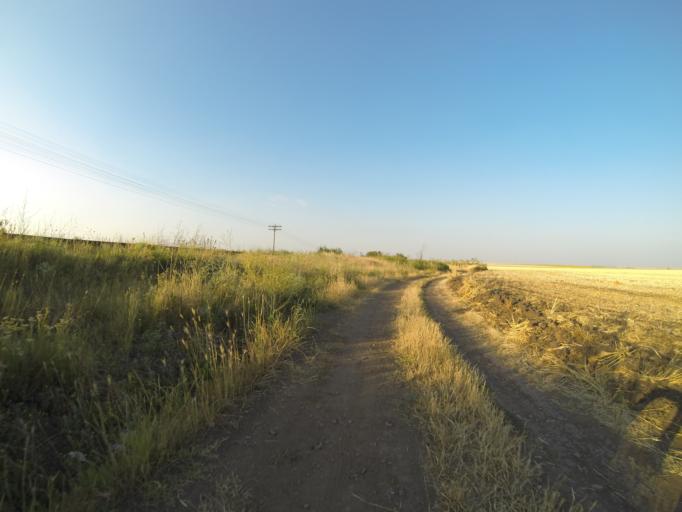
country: RO
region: Dolj
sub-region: Comuna Ceratu
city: Ceratu
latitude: 44.0523
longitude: 23.6720
